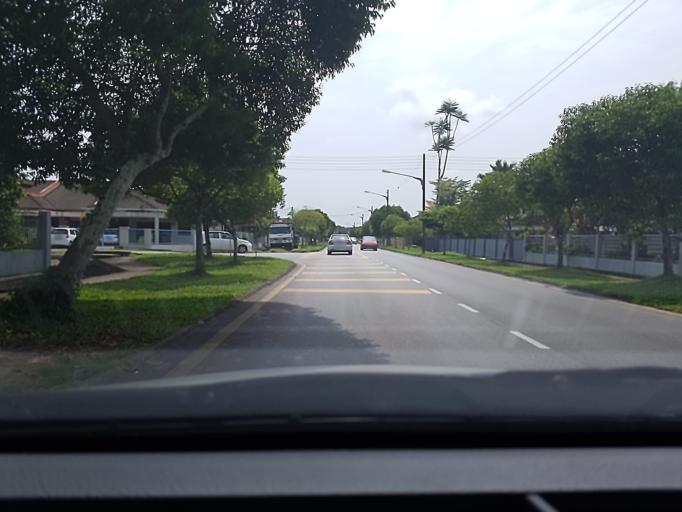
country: MY
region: Sarawak
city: Kuching
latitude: 1.5144
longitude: 110.3622
